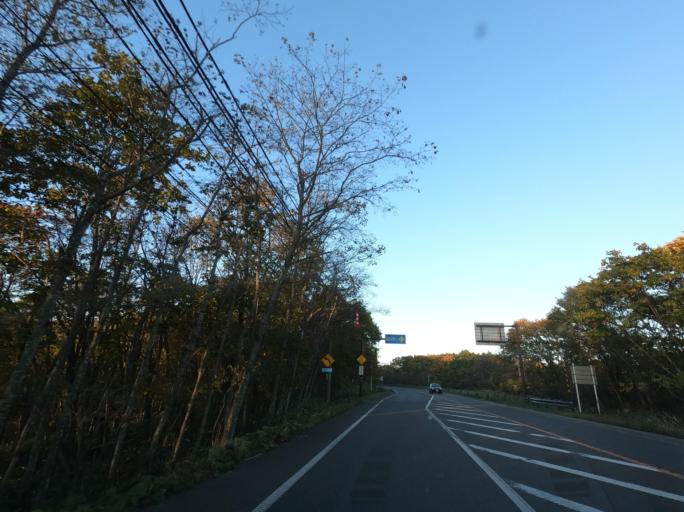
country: JP
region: Hokkaido
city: Kushiro
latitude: 43.0748
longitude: 144.3203
